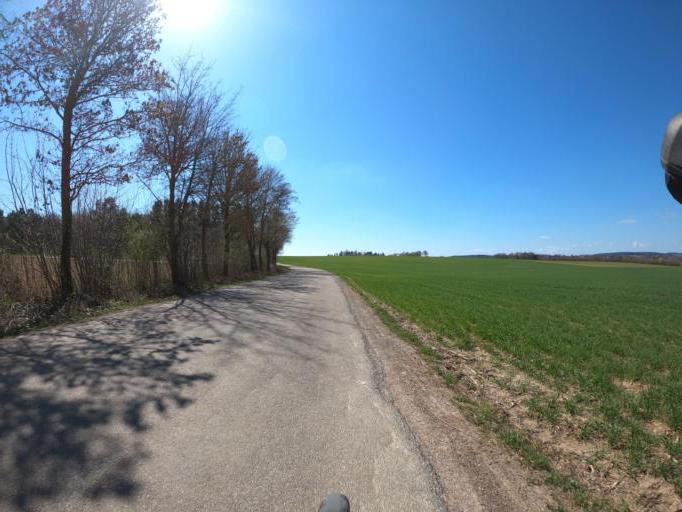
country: DE
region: Baden-Wuerttemberg
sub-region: Karlsruhe Region
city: Horb am Neckar
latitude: 48.4247
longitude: 8.6910
